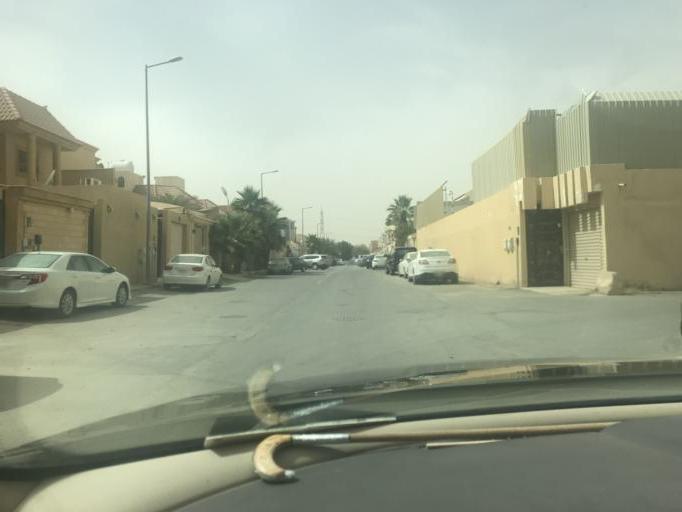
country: SA
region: Ar Riyad
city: Riyadh
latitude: 24.7912
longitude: 46.6900
